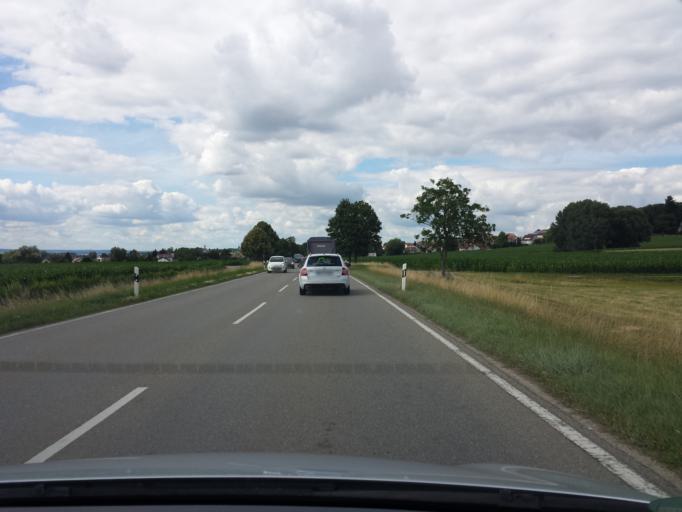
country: DE
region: Baden-Wuerttemberg
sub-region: Tuebingen Region
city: Burgrieden
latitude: 48.2174
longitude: 9.9577
